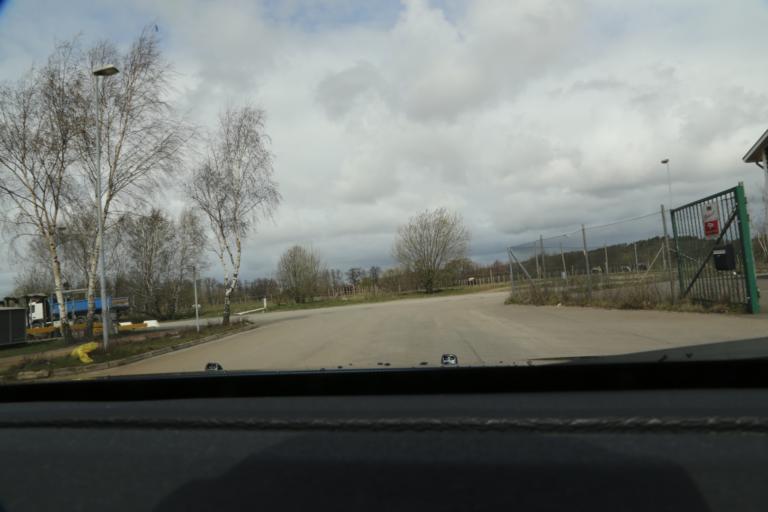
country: SE
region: Halland
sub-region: Varbergs Kommun
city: Varberg
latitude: 57.1278
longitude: 12.2882
